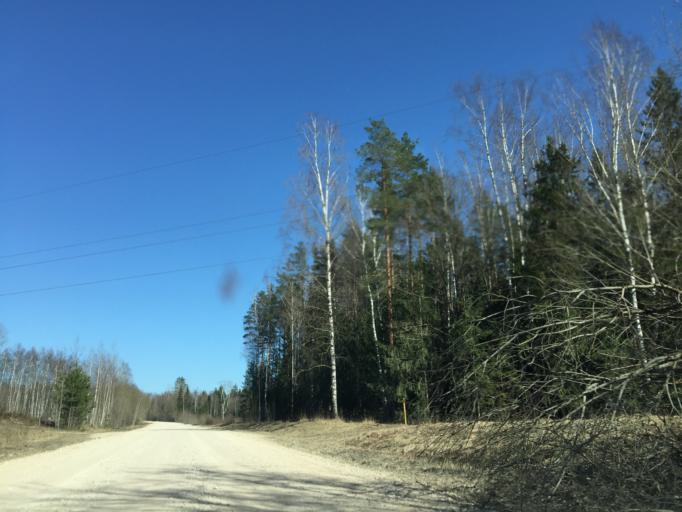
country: LV
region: Malpils
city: Malpils
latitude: 57.0285
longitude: 25.0351
